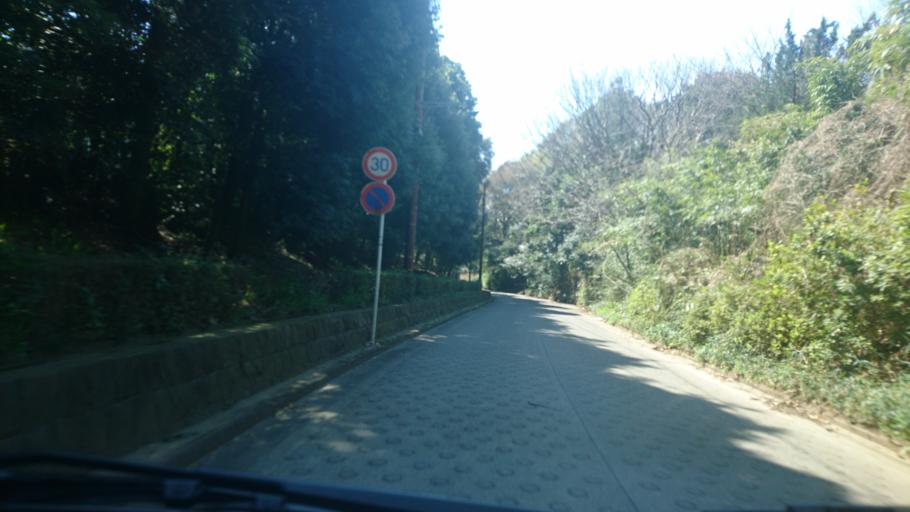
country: JP
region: Kanagawa
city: Fujisawa
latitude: 35.3871
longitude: 139.4249
